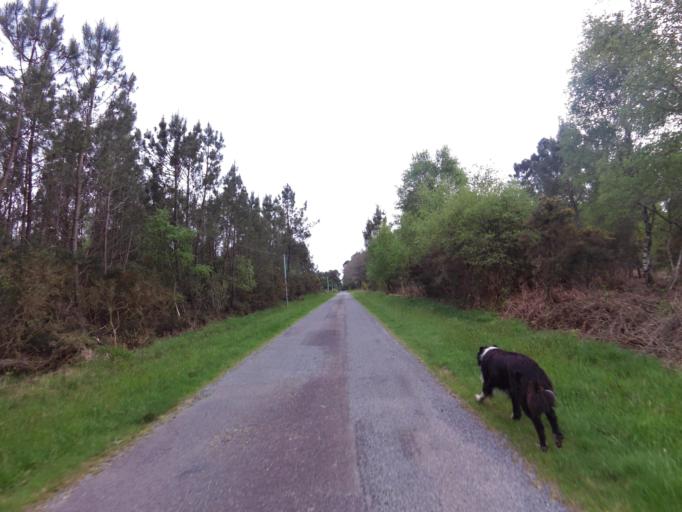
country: FR
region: Brittany
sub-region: Departement du Morbihan
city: Molac
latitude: 47.7462
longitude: -2.4211
